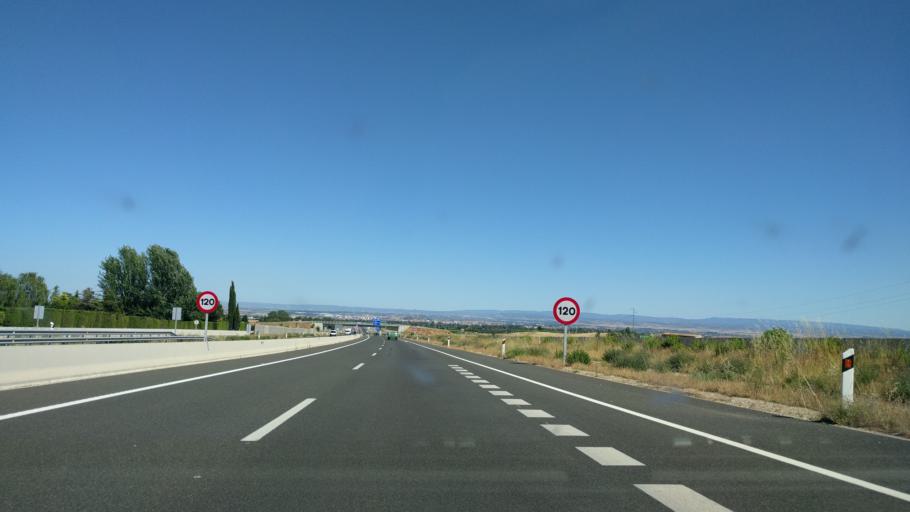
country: ES
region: Catalonia
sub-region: Provincia de Lleida
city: Alpicat
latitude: 41.6572
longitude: 0.5361
